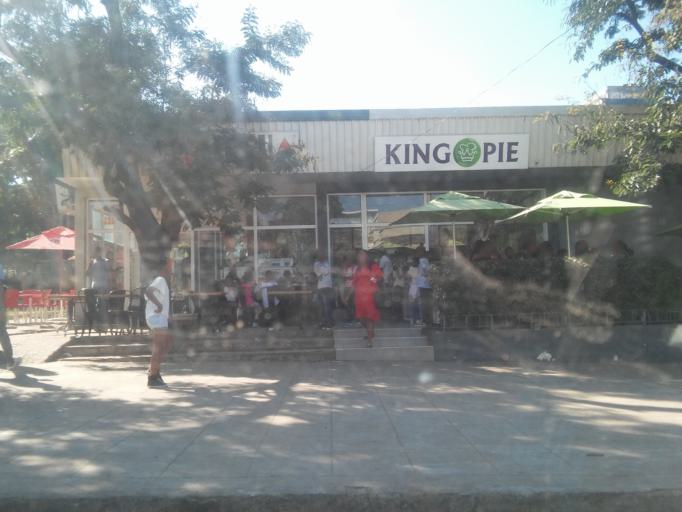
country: MZ
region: Maputo City
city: Maputo
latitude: -25.9626
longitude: 32.5685
